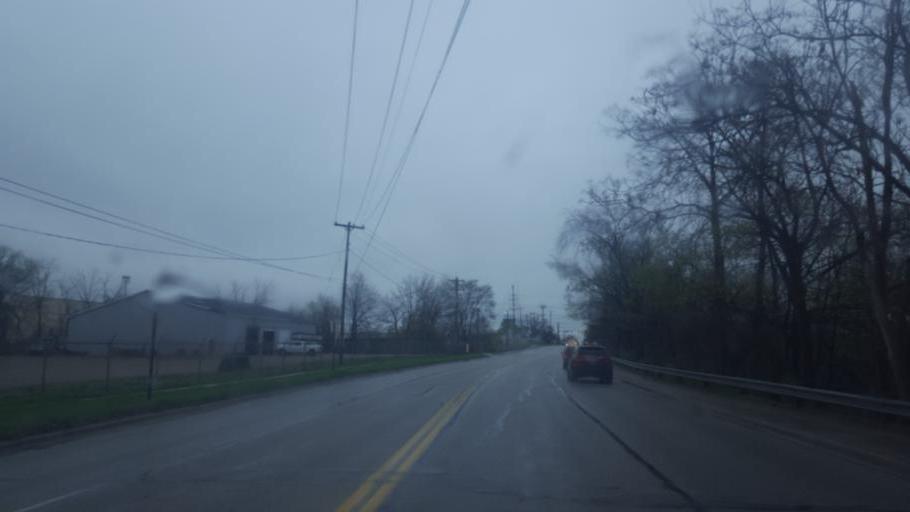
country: US
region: Michigan
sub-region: Isabella County
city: Mount Pleasant
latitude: 43.6118
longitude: -84.7809
